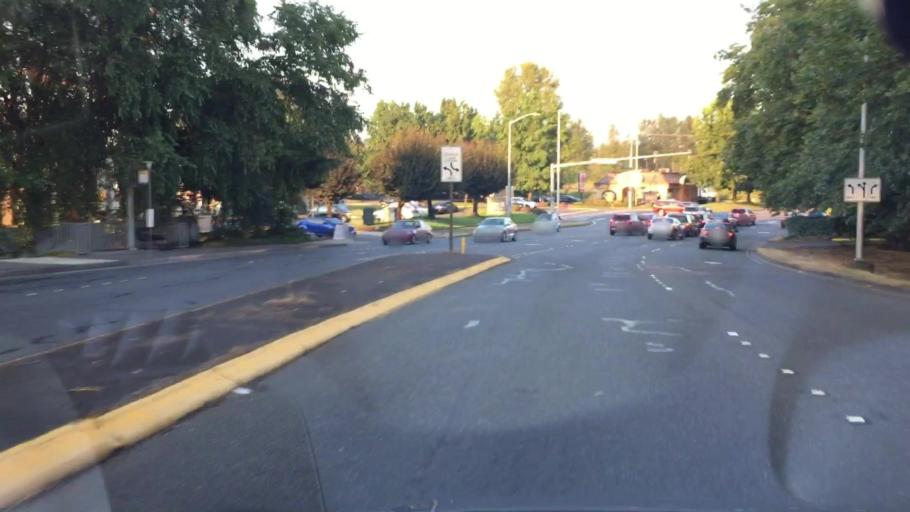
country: US
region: Washington
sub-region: King County
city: Tukwila
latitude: 47.4565
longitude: -122.2453
